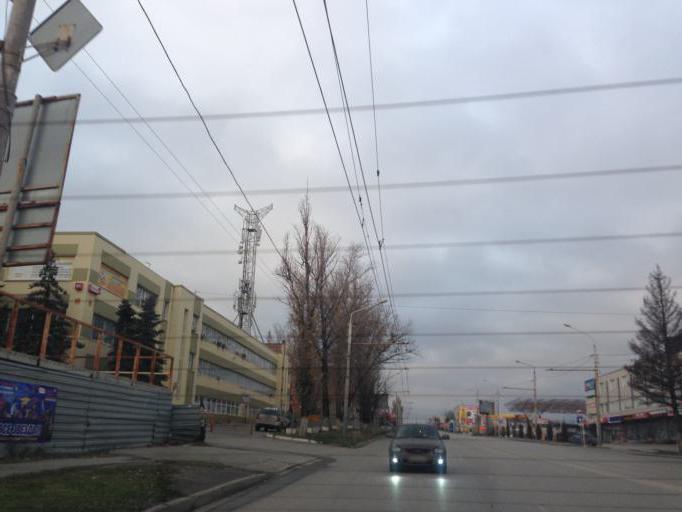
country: RU
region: Rostov
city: Severnyy
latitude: 47.2771
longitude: 39.6857
